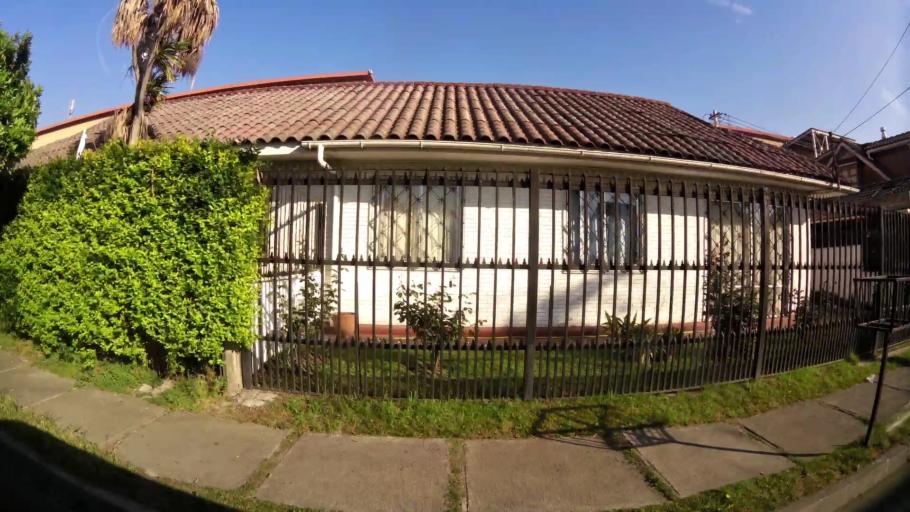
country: CL
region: Santiago Metropolitan
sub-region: Provincia de Santiago
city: Lo Prado
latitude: -33.4837
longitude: -70.7497
